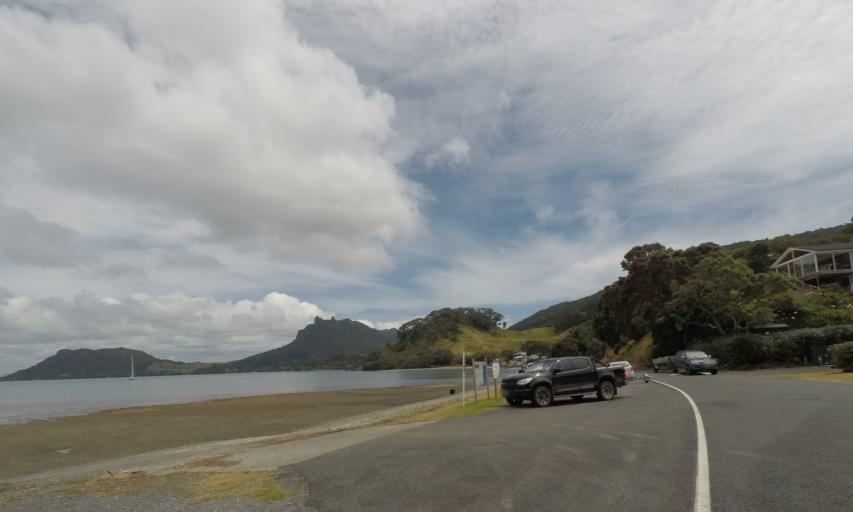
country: NZ
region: Northland
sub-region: Whangarei
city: Ruakaka
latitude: -35.8446
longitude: 174.5367
